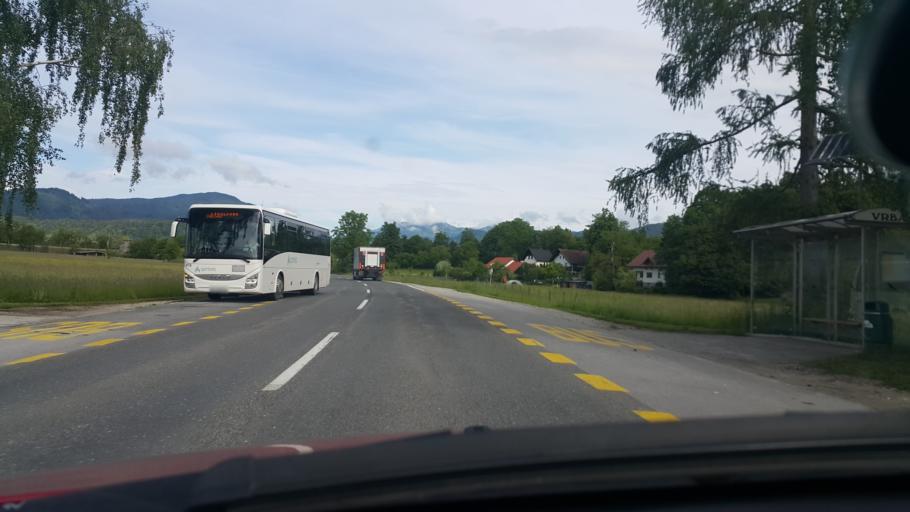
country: SI
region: Zirovnica
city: Zirovnica
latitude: 46.3875
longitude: 14.1456
